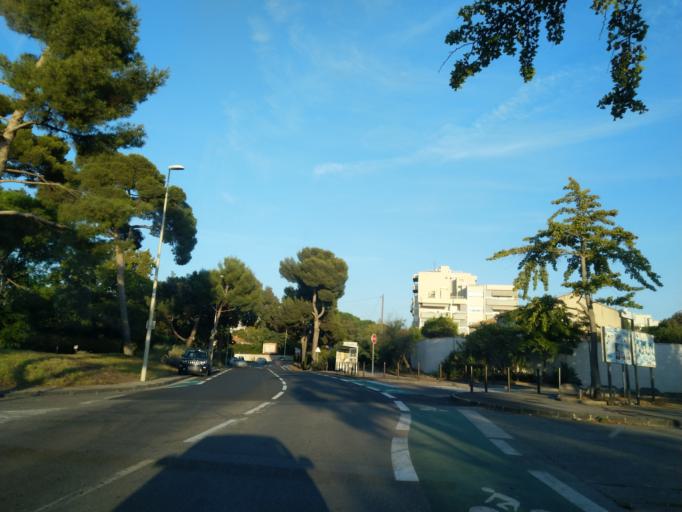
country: FR
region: Provence-Alpes-Cote d'Azur
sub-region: Departement des Bouches-du-Rhone
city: Marseille 09
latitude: 43.2459
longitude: 5.3930
